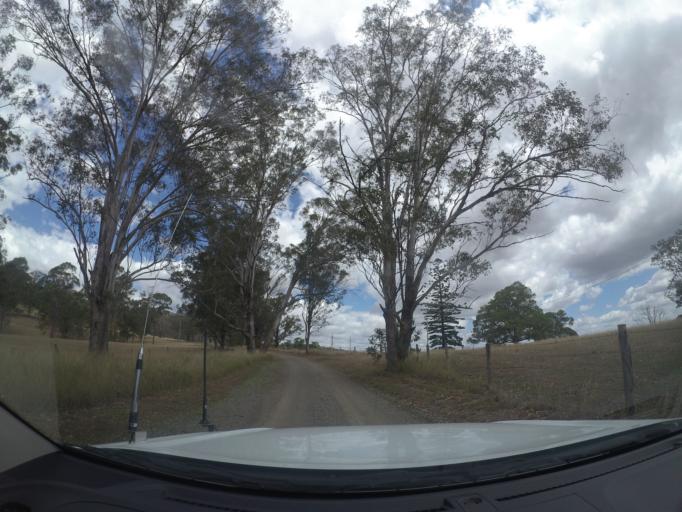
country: AU
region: Queensland
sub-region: Logan
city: Cedar Vale
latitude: -27.9153
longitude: 153.0309
